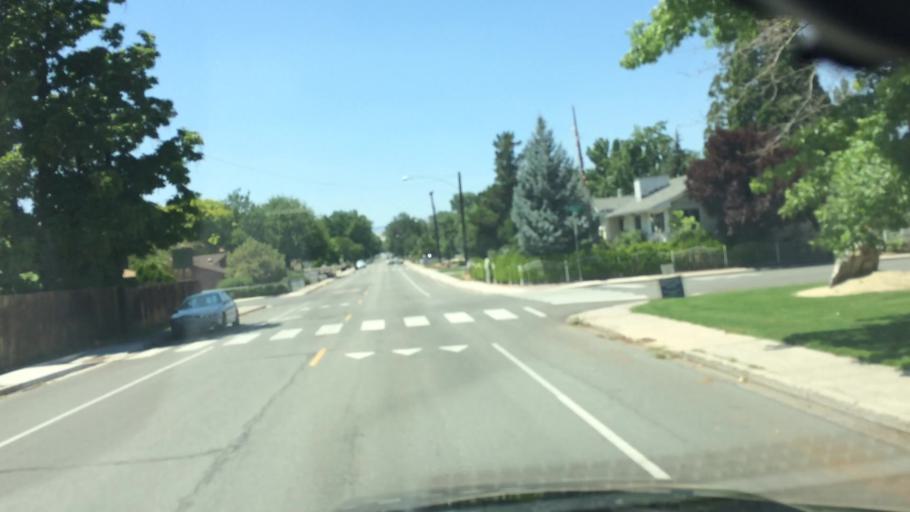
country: US
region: Nevada
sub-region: Washoe County
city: Sparks
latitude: 39.5472
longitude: -119.7386
